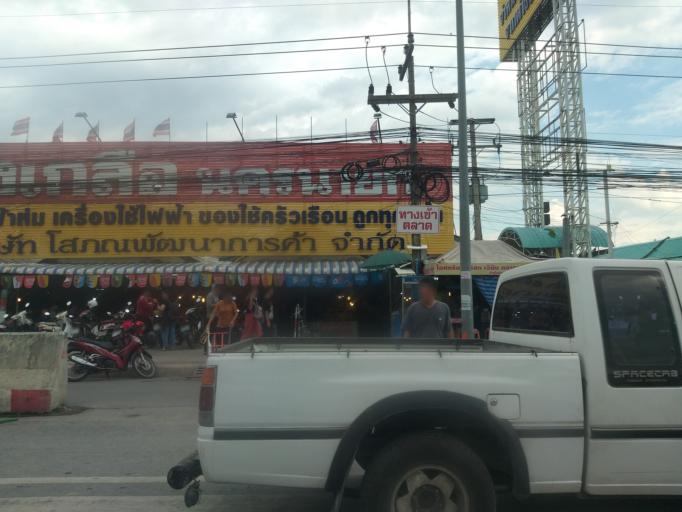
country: TH
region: Nakhon Nayok
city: Nakhon Nayok
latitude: 14.2344
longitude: 101.2421
